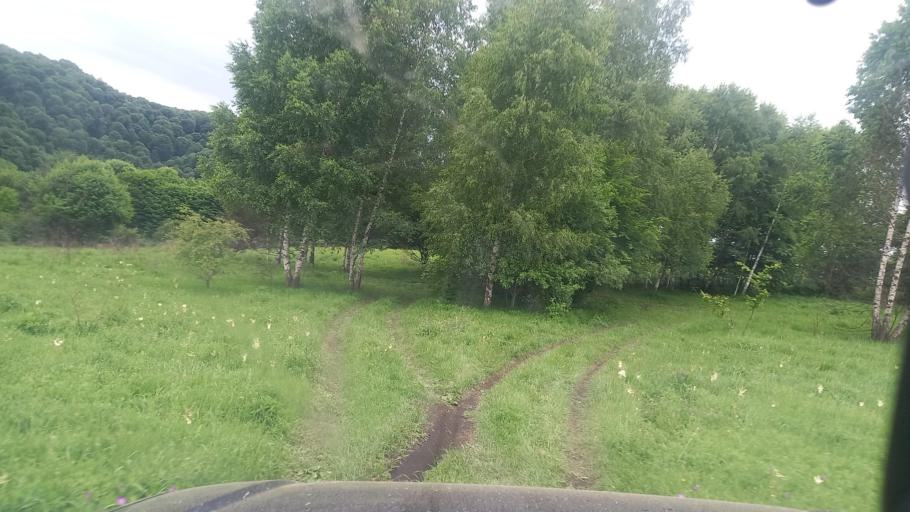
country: RU
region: Karachayevo-Cherkesiya
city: Pregradnaya
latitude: 44.0341
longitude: 41.3156
